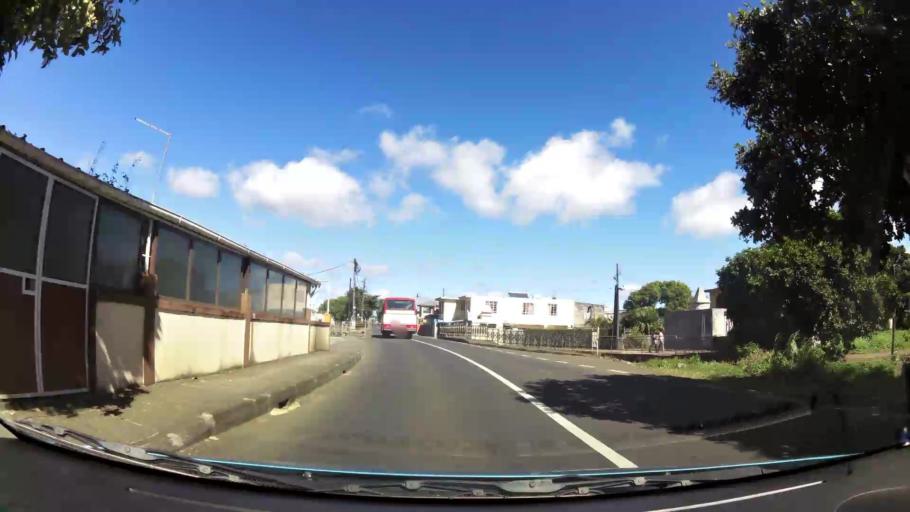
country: MU
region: Plaines Wilhems
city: Vacoas
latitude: -20.3288
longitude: 57.4769
